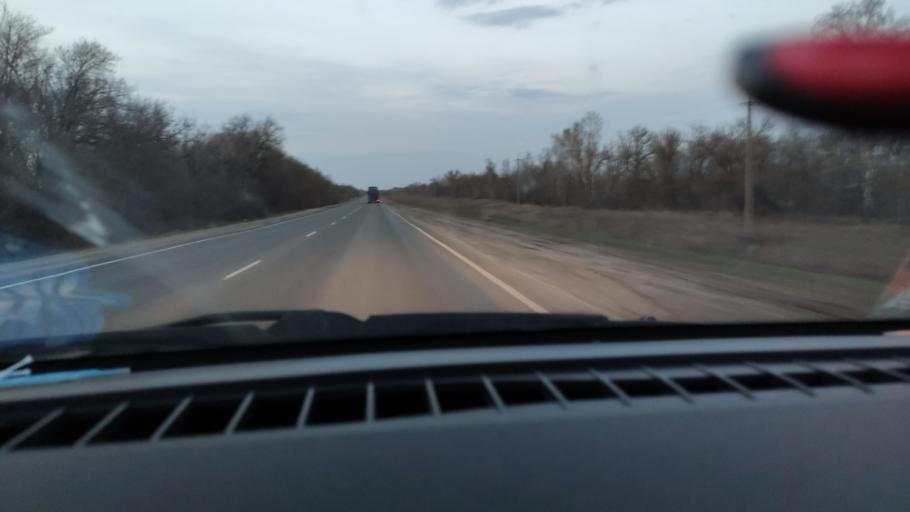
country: RU
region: Saratov
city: Sinodskoye
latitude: 52.0308
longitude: 46.7219
